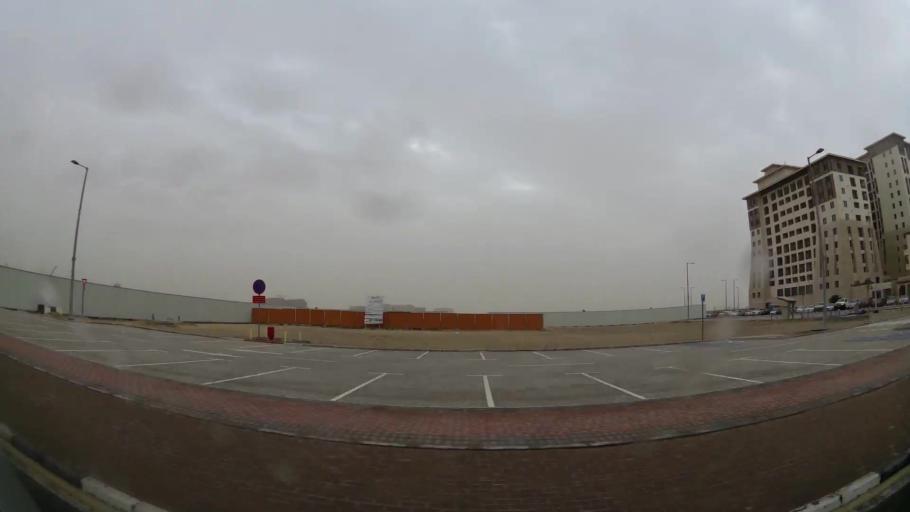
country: AE
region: Abu Dhabi
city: Abu Dhabi
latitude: 24.4444
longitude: 54.6116
